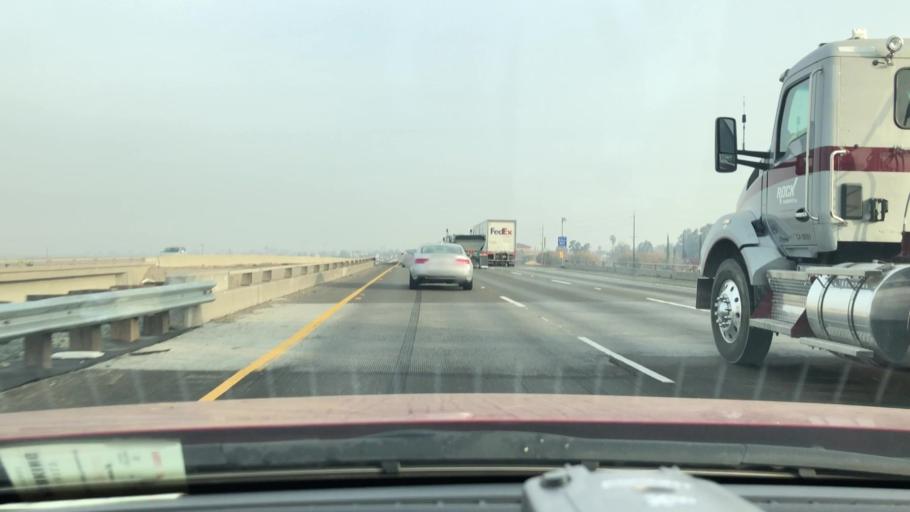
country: US
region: California
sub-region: San Joaquin County
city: Lathrop
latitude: 37.8260
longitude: -121.2901
